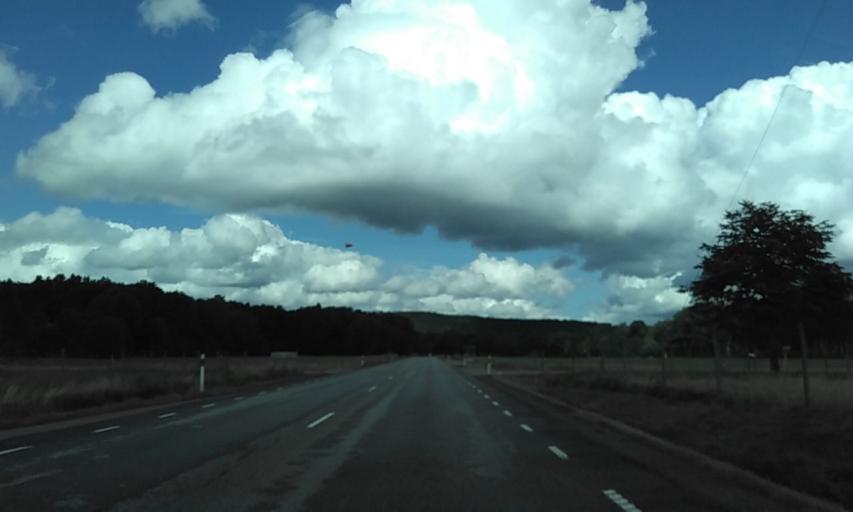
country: SE
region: Vaestra Goetaland
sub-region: Alingsas Kommun
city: Ingared
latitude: 57.9538
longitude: 12.3954
